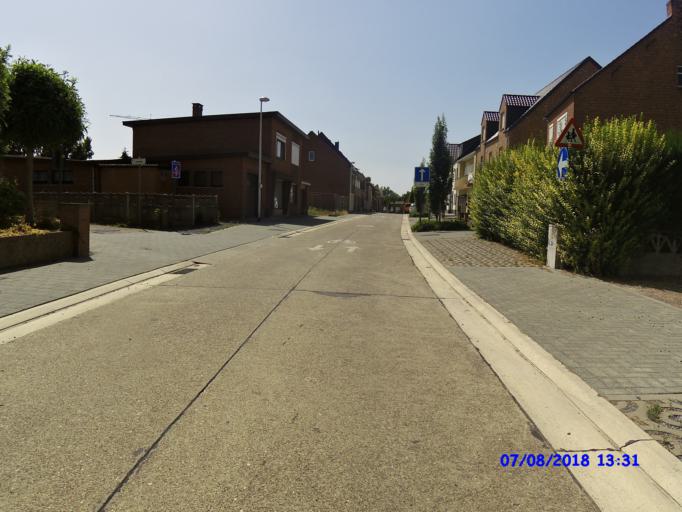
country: BE
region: Flanders
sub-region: Provincie Antwerpen
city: Laakdal
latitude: 51.0675
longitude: 4.9860
